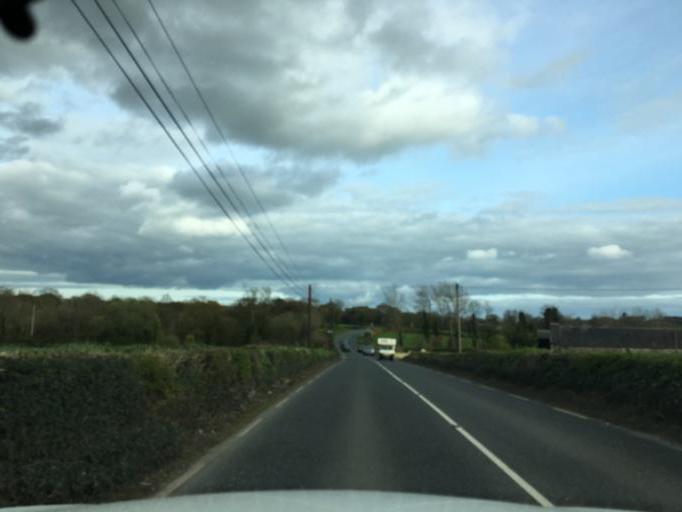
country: IE
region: Leinster
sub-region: Loch Garman
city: New Ross
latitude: 52.4342
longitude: -6.9584
